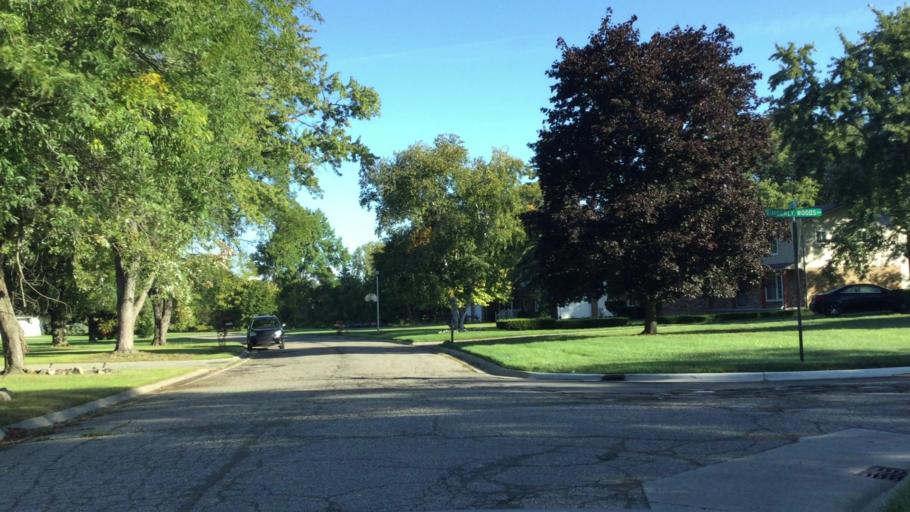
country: US
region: Michigan
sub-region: Genesee County
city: Beecher
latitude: 43.0839
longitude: -83.7553
